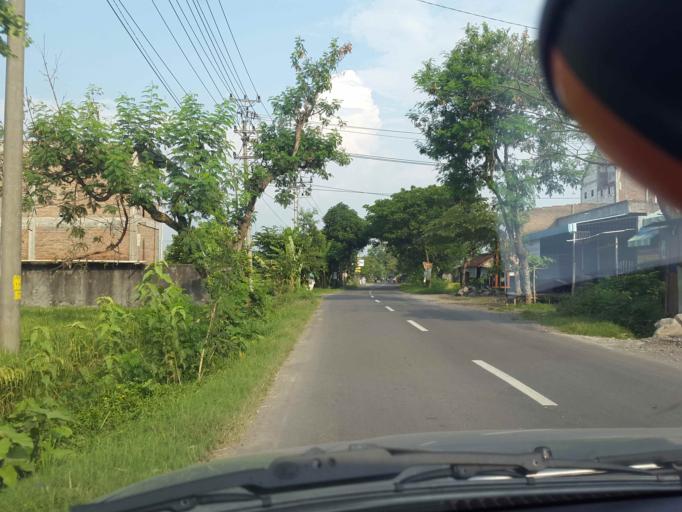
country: ID
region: Central Java
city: Jaten
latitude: -7.5695
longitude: 110.9034
